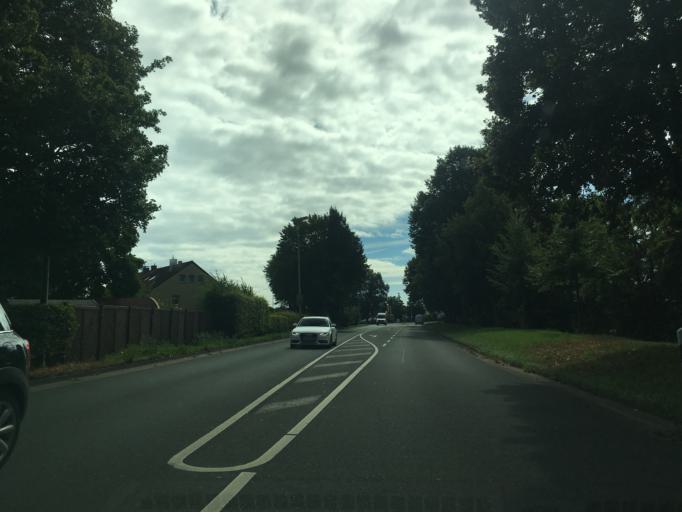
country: DE
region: Lower Saxony
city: Hameln
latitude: 52.1182
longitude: 9.3401
